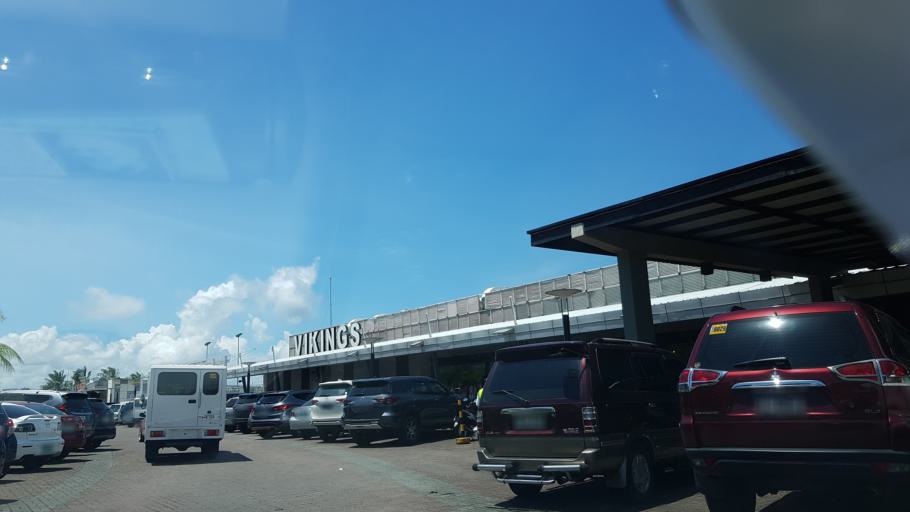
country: PH
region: Metro Manila
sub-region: City of Manila
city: Port Area
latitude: 14.5410
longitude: 120.9794
